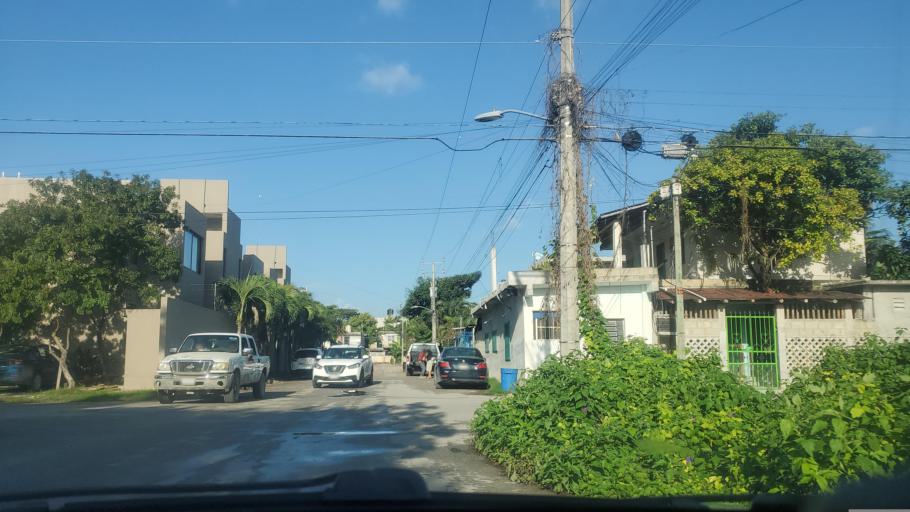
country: MX
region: Quintana Roo
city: Tulum
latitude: 20.2133
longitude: -87.4694
